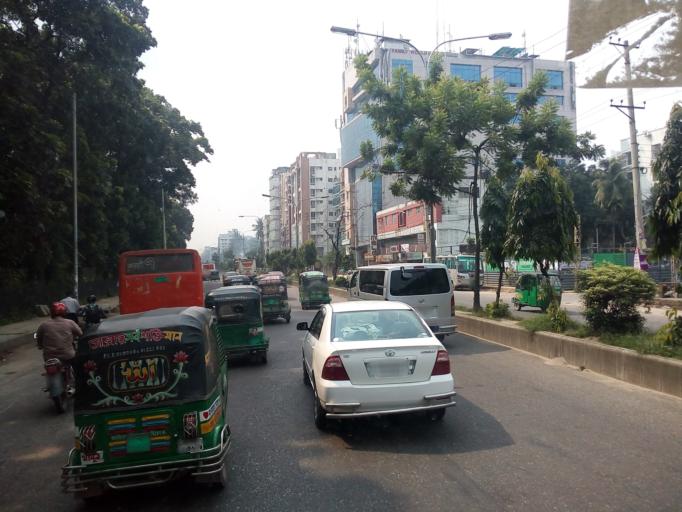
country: BD
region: Dhaka
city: Azimpur
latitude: 23.7639
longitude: 90.3710
